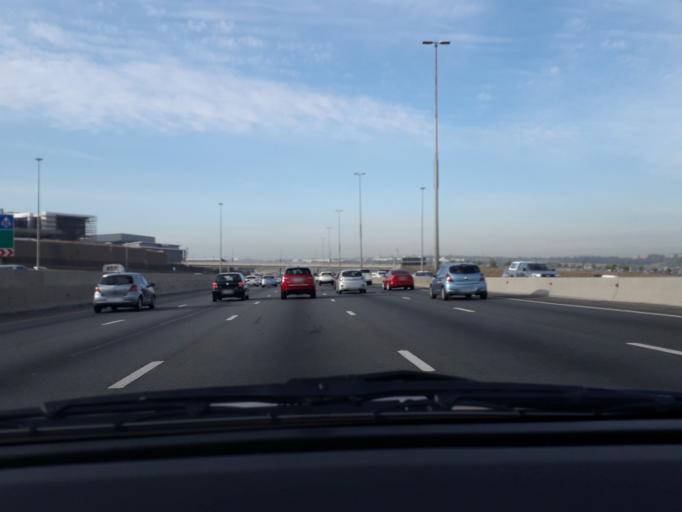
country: ZA
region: Gauteng
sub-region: City of Johannesburg Metropolitan Municipality
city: Midrand
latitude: -26.0165
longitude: 28.1153
